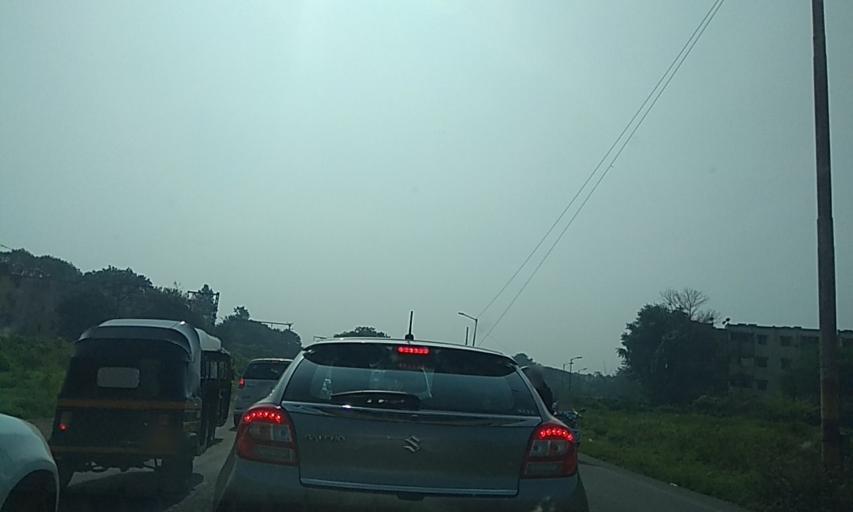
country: IN
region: Maharashtra
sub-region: Pune Division
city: Khadki
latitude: 18.5579
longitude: 73.8438
